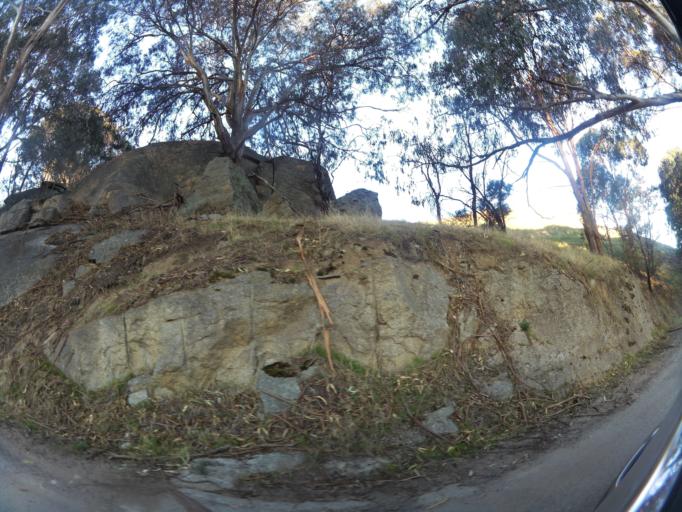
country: AU
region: Victoria
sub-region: Murrindindi
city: Alexandra
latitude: -37.1381
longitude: 145.5184
